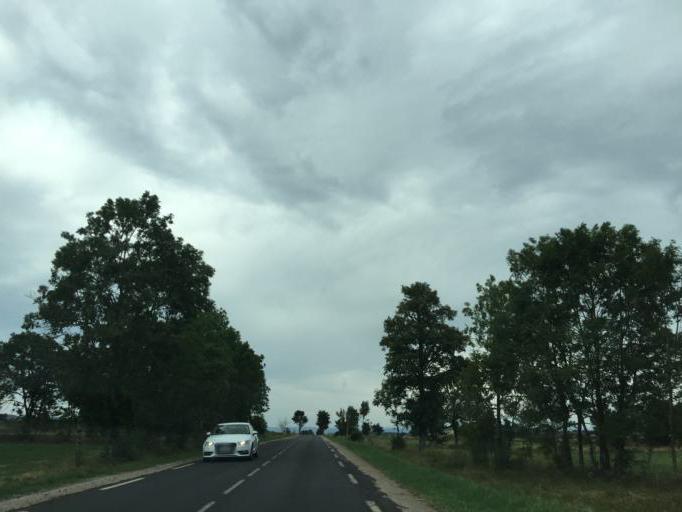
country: FR
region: Auvergne
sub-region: Departement de la Haute-Loire
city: Solignac-sur-Loire
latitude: 44.8568
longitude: 3.8432
